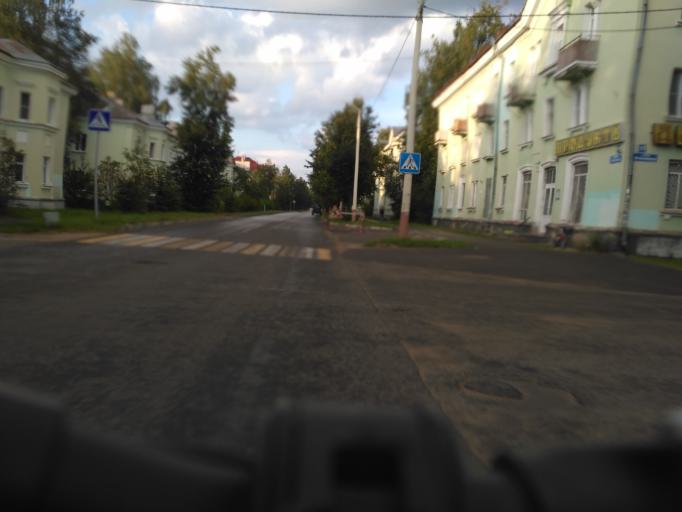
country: RU
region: Moskovskaya
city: Dubna
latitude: 56.7461
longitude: 37.1972
